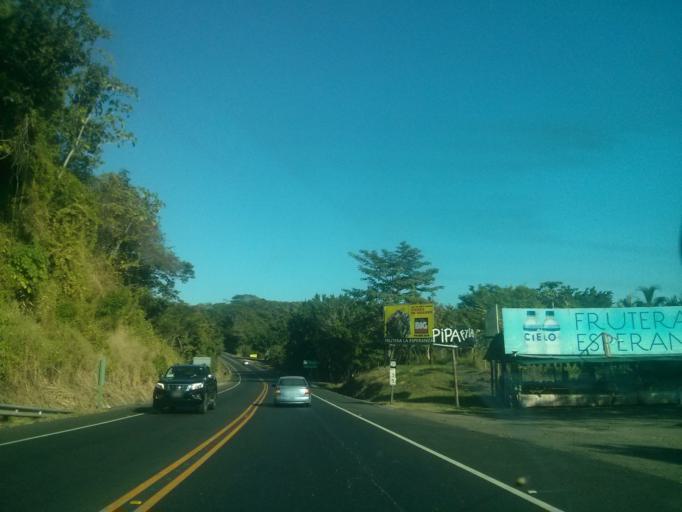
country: CR
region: Alajuela
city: Orotina
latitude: 9.8996
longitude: -84.5379
